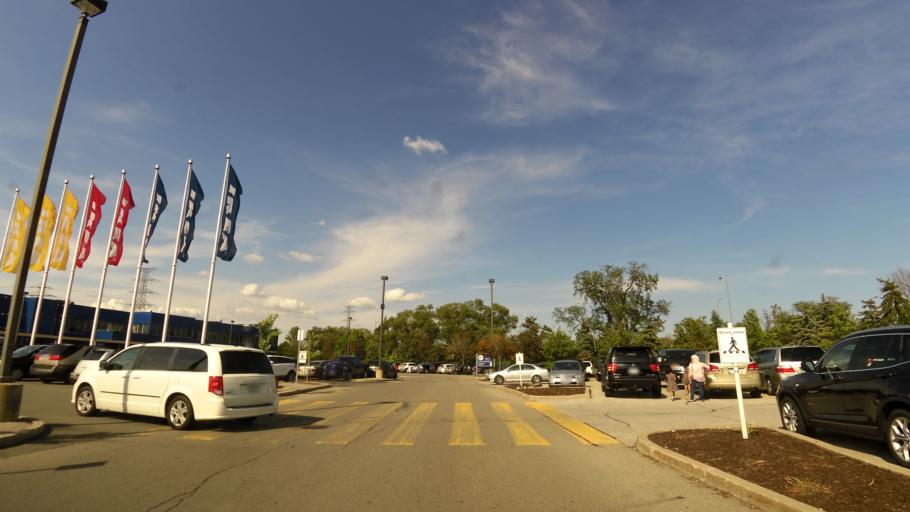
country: CA
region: Ontario
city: Burlington
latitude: 43.3269
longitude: -79.8285
